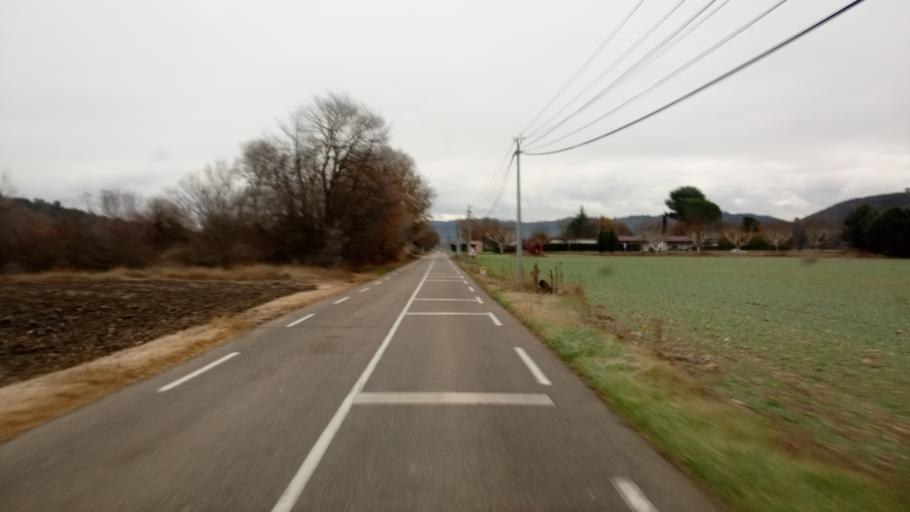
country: FR
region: Provence-Alpes-Cote d'Azur
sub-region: Departement du Var
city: Vinon-sur-Verdon
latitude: 43.7276
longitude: 5.8244
